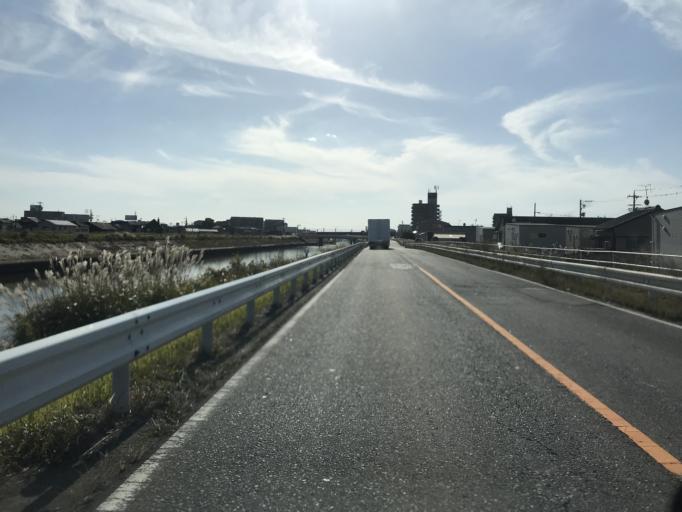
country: JP
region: Aichi
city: Nagoya-shi
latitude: 35.2097
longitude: 136.8600
